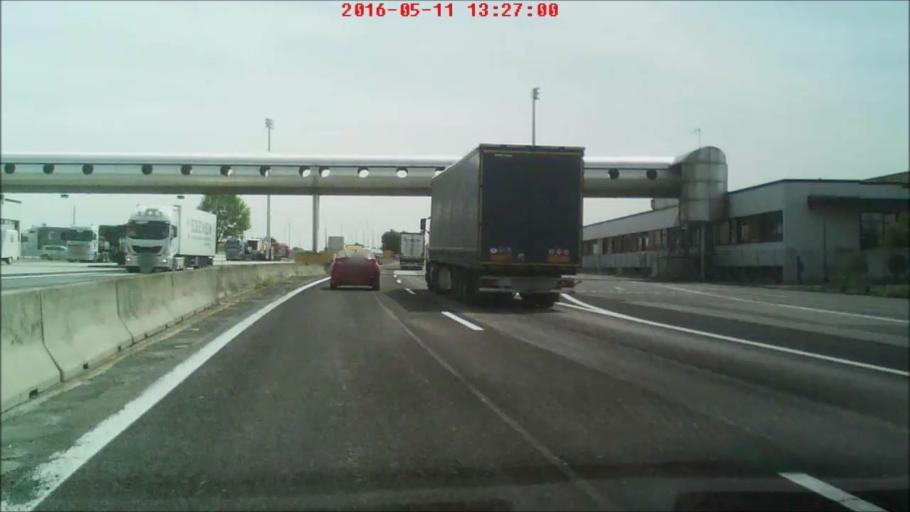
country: AT
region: Upper Austria
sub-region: Politischer Bezirk Scharding
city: Sankt Marienkirchen bei Schaerding
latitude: 48.4072
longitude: 13.4281
